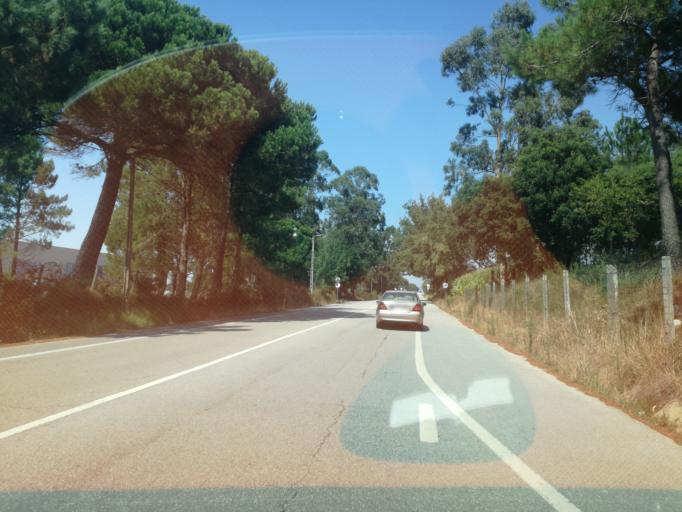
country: PT
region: Braga
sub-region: Esposende
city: Apulia
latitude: 41.4565
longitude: -8.7505
